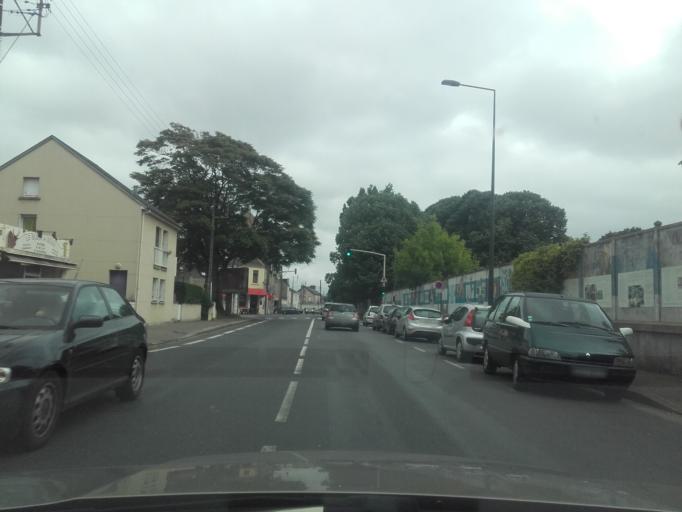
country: FR
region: Centre
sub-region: Departement d'Indre-et-Loire
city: Tours
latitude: 47.3830
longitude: 0.7034
